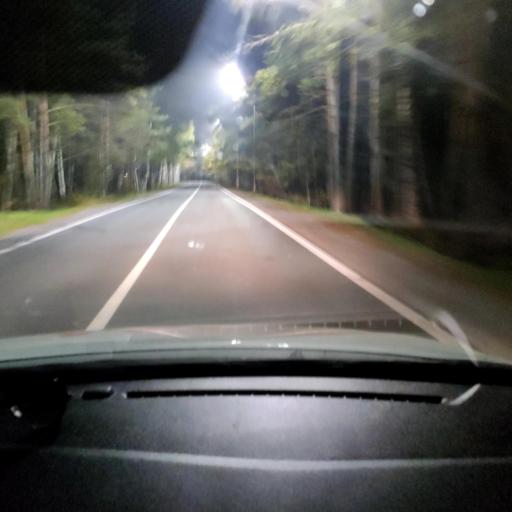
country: RU
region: Tatarstan
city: Verkhniy Uslon
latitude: 55.6316
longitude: 49.0170
